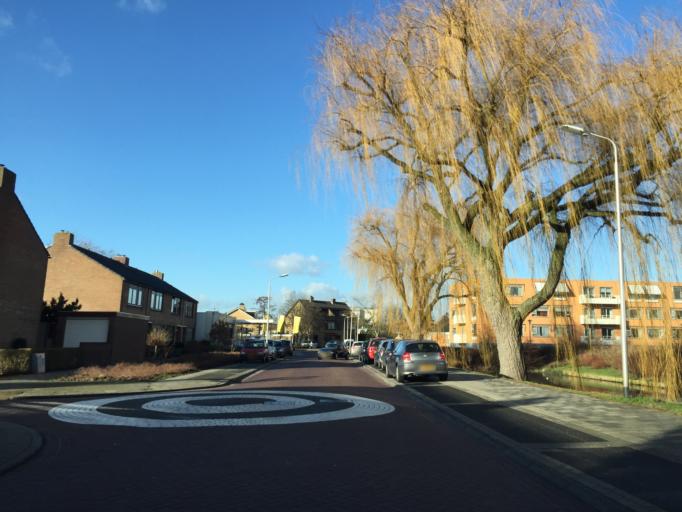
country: NL
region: South Holland
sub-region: Gemeente Lansingerland
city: Berkel en Rodenrijs
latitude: 51.9909
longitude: 4.4796
